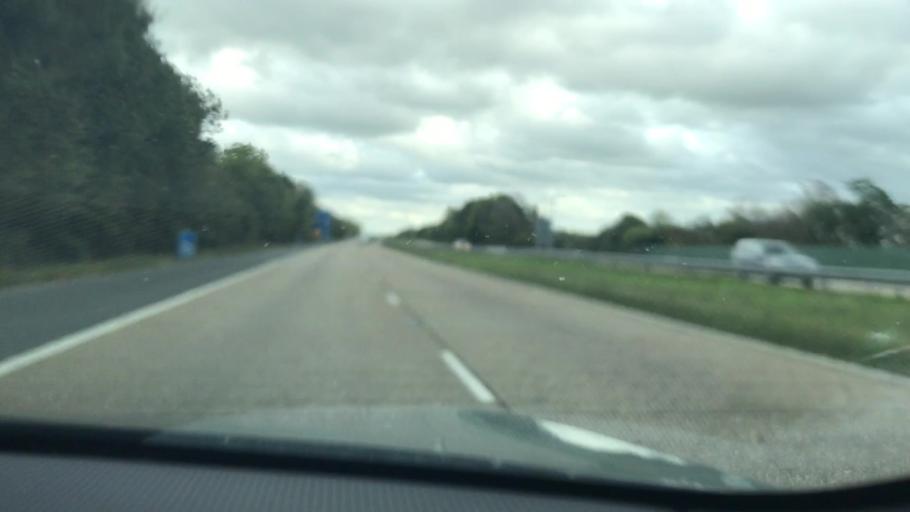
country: GB
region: England
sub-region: Wokingham
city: Winnersh
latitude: 51.4355
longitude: -0.8651
